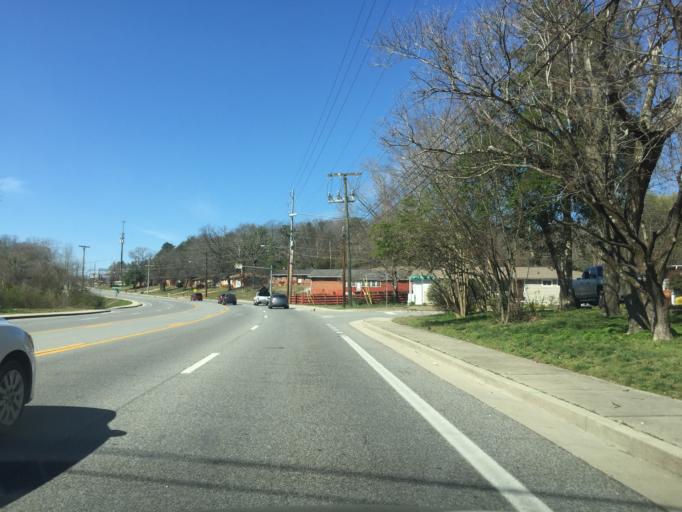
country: US
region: Tennessee
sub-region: Hamilton County
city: Red Bank
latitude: 35.1172
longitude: -85.2673
